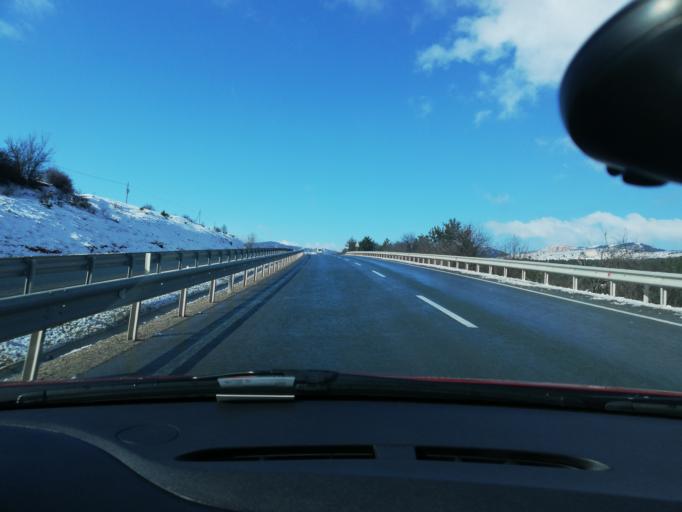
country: TR
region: Kastamonu
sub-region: Cide
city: Kastamonu
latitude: 41.3677
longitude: 33.7476
